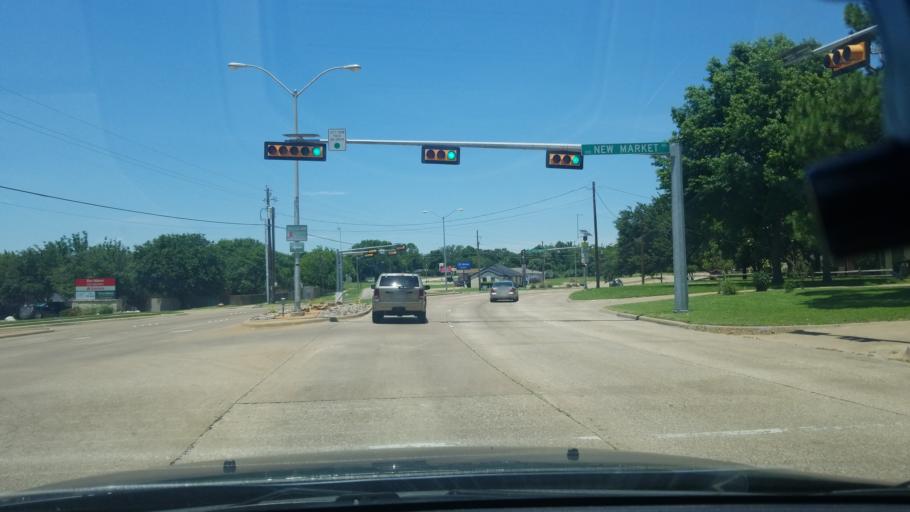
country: US
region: Texas
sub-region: Dallas County
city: Mesquite
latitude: 32.7558
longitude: -96.5970
